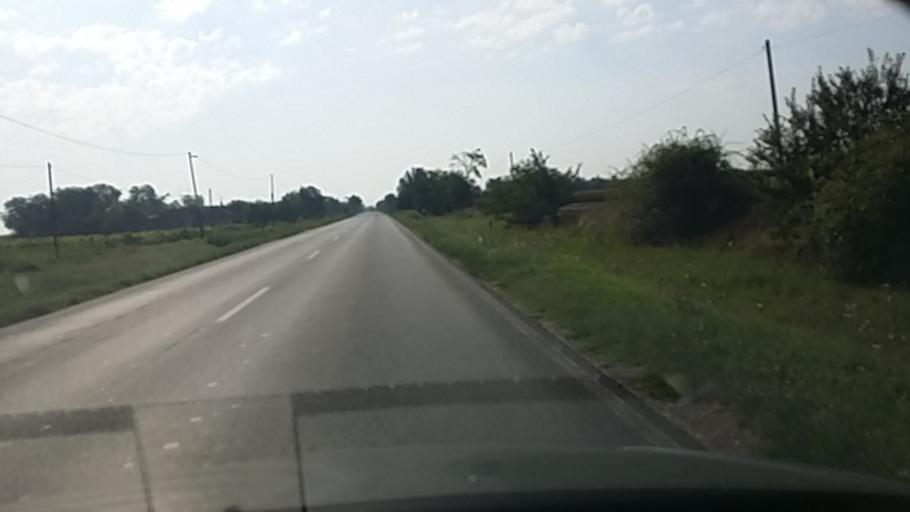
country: HU
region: Bekes
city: Kondoros
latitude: 46.7917
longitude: 20.7319
